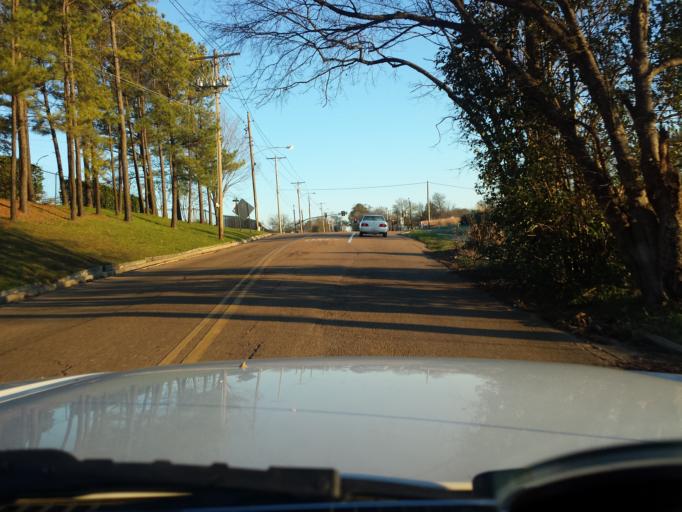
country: US
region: Mississippi
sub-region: Hinds County
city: Jackson
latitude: 32.3026
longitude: -90.1770
